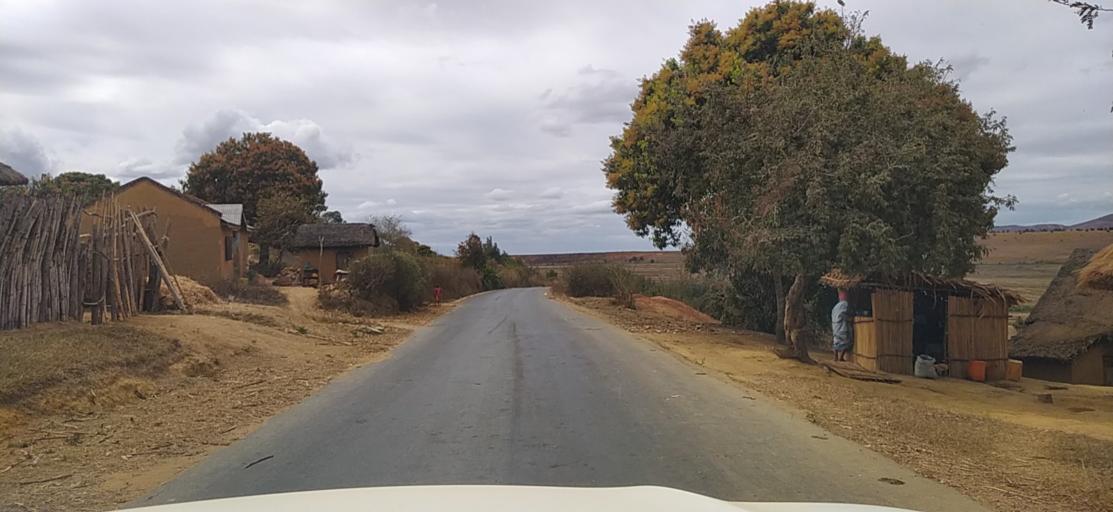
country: MG
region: Alaotra Mangoro
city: Ambatondrazaka
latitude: -17.9282
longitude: 48.2573
